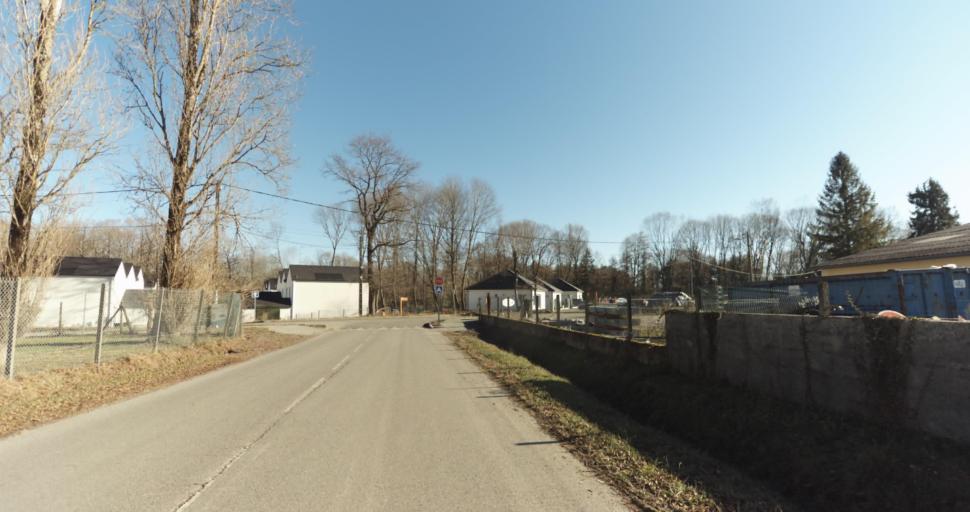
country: FR
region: Aquitaine
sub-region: Departement des Pyrenees-Atlantiques
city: Buros
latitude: 43.3287
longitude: -0.3000
